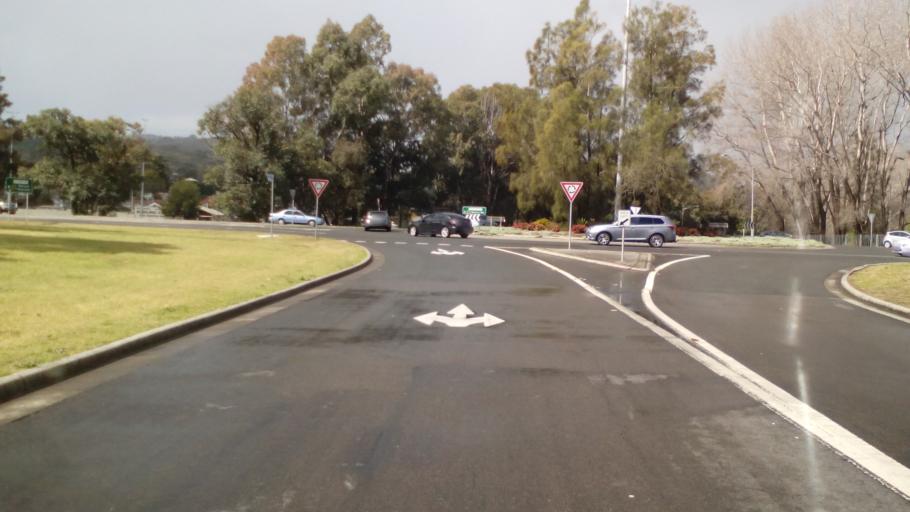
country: AU
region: New South Wales
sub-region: Lake Macquarie Shire
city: Glendale
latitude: -32.9571
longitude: 151.6165
